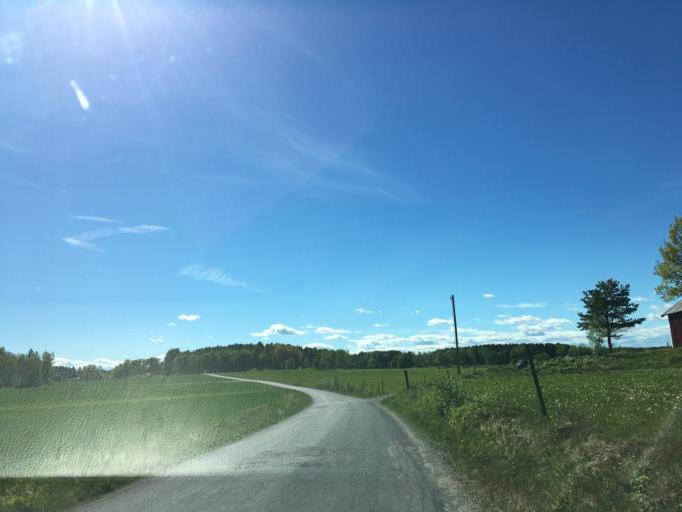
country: SE
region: Soedermanland
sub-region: Eskilstuna Kommun
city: Hallbybrunn
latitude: 59.3554
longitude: 16.4314
